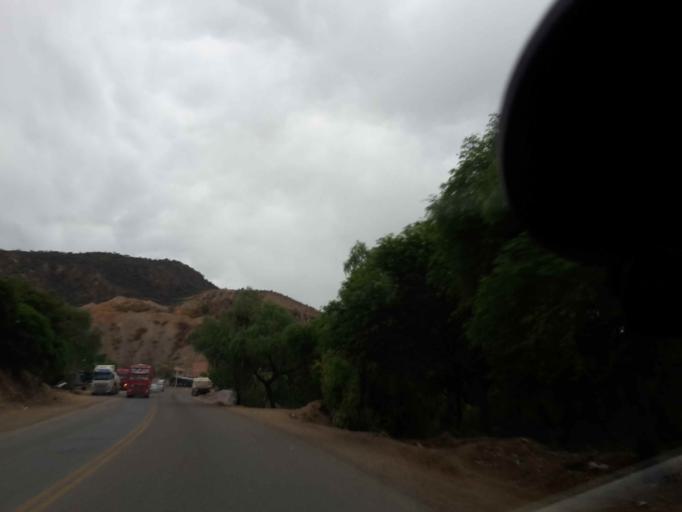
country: BO
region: Cochabamba
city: Sipe Sipe
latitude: -17.5570
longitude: -66.3420
